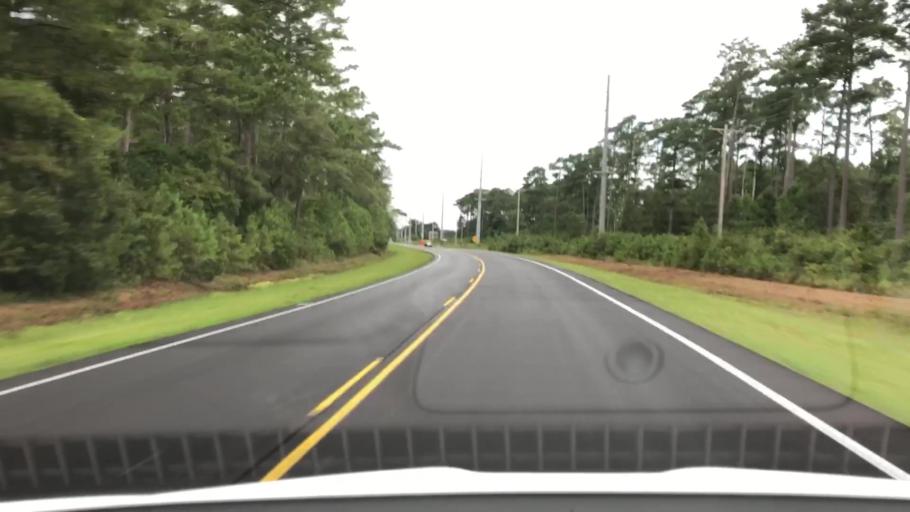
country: US
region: North Carolina
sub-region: Onslow County
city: Swansboro
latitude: 34.7860
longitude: -77.1180
